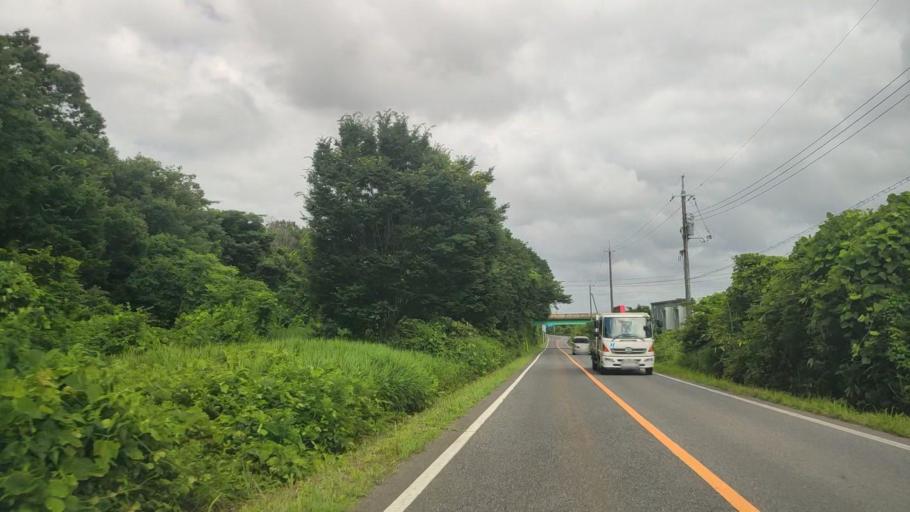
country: JP
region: Tottori
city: Yonago
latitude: 35.4204
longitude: 133.4360
